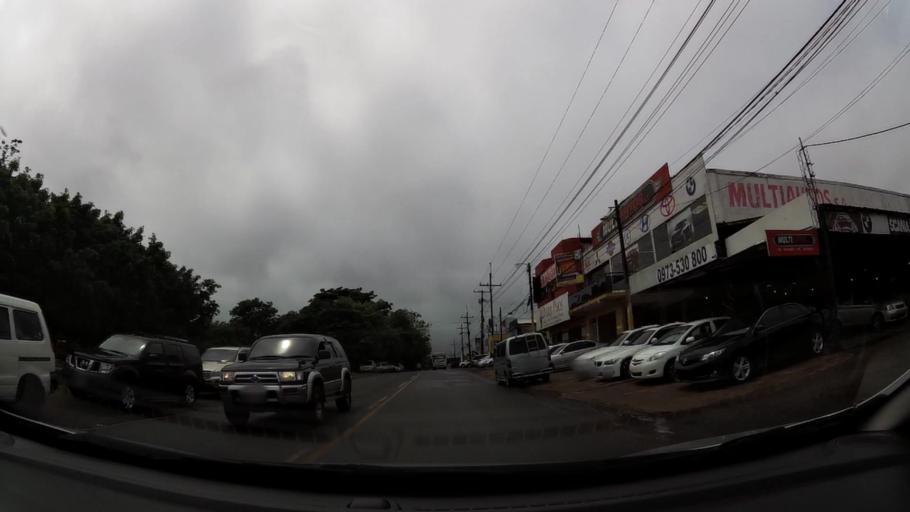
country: PY
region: Alto Parana
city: Ciudad del Este
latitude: -25.5016
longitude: -54.6565
